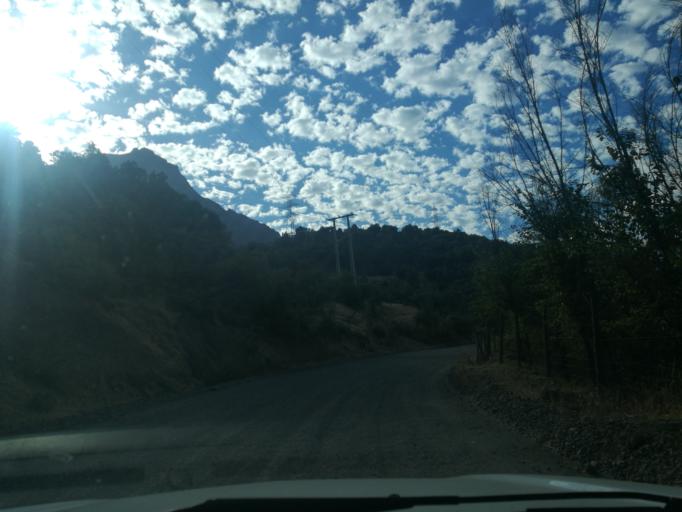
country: CL
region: O'Higgins
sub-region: Provincia de Cachapoal
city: Machali
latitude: -34.2708
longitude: -70.4537
